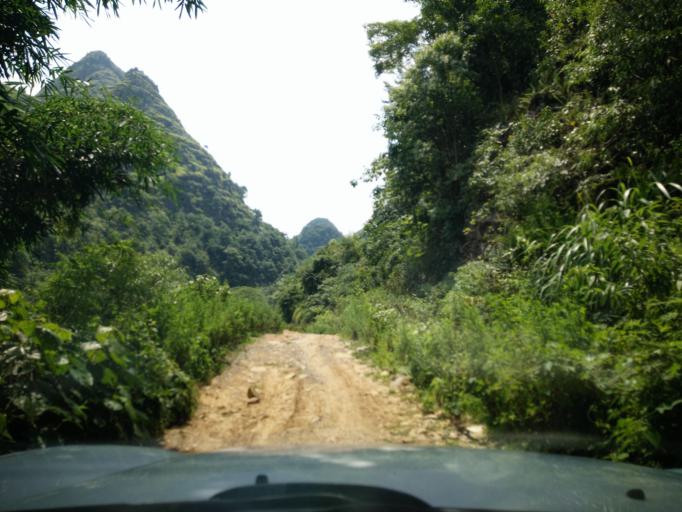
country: CN
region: Guangxi Zhuangzu Zizhiqu
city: Xinzhou
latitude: 25.0138
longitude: 105.7039
